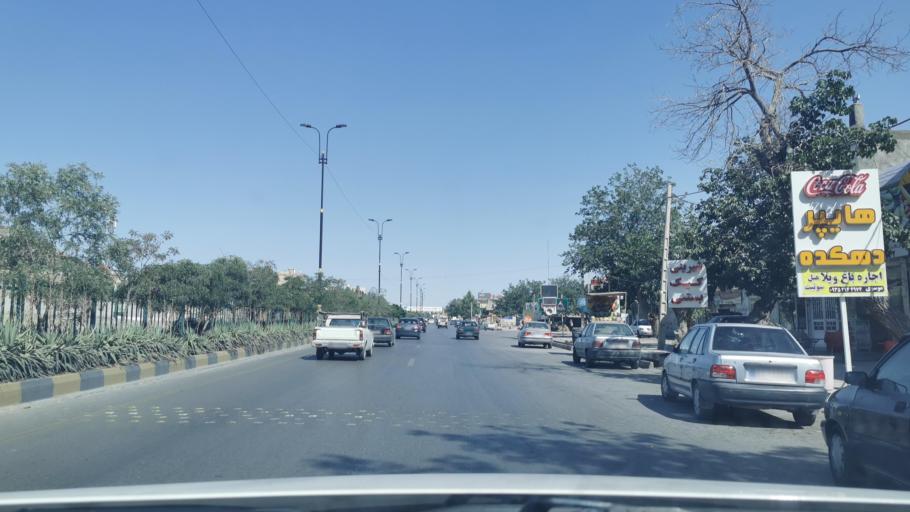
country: IR
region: Razavi Khorasan
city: Torqabeh
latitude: 36.3988
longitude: 59.3927
